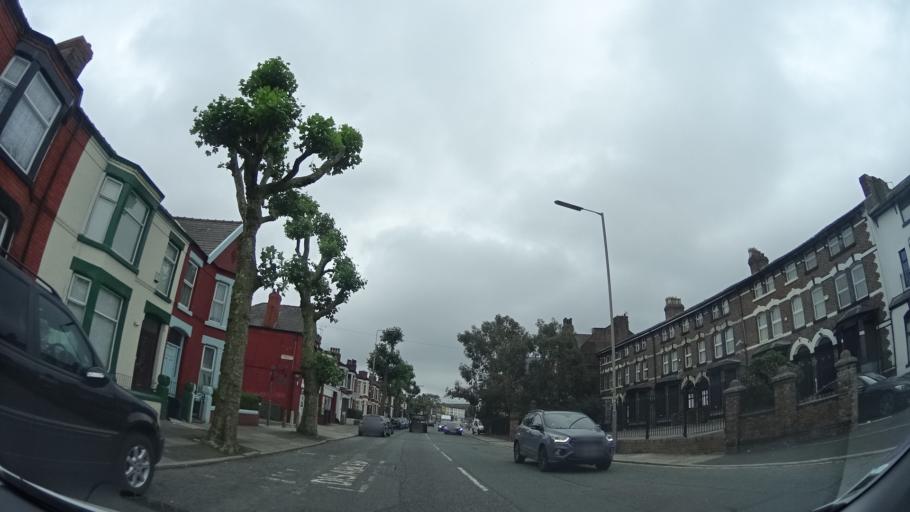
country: GB
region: England
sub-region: Liverpool
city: Liverpool
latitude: 53.4156
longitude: -2.9145
